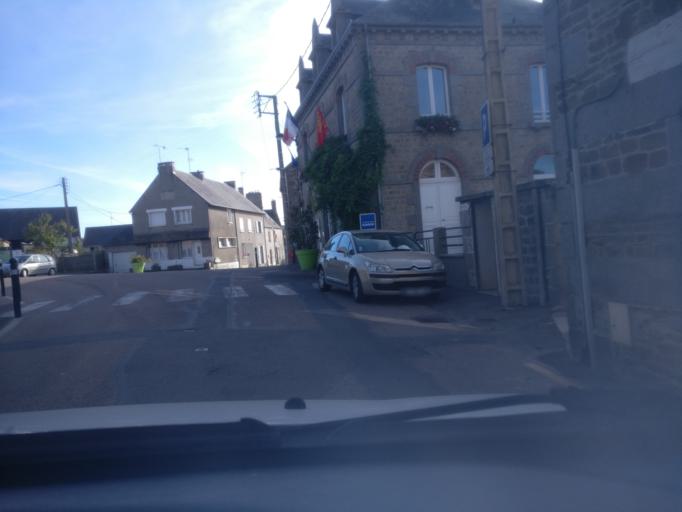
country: FR
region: Lower Normandy
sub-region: Departement de la Manche
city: Marcey-les-Greves
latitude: 48.7009
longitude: -1.4415
